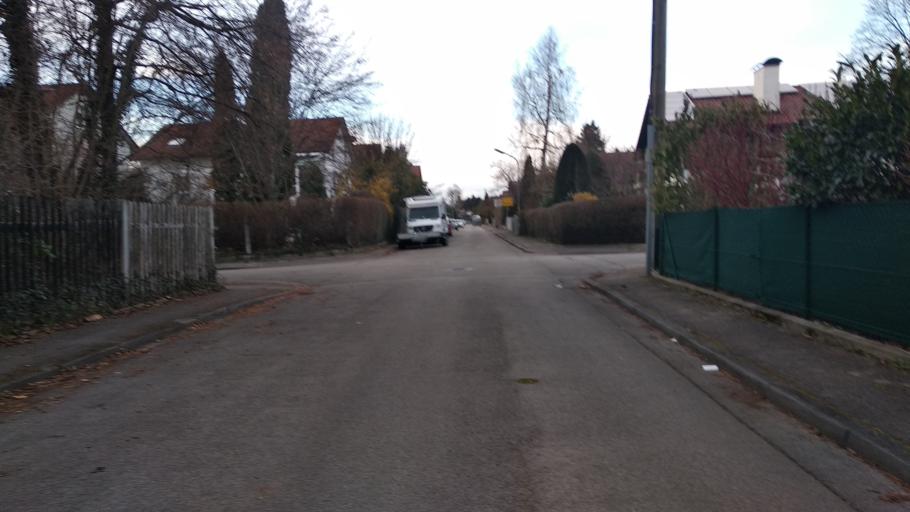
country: DE
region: Bavaria
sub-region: Upper Bavaria
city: Ottobrunn
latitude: 48.0776
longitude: 11.6798
